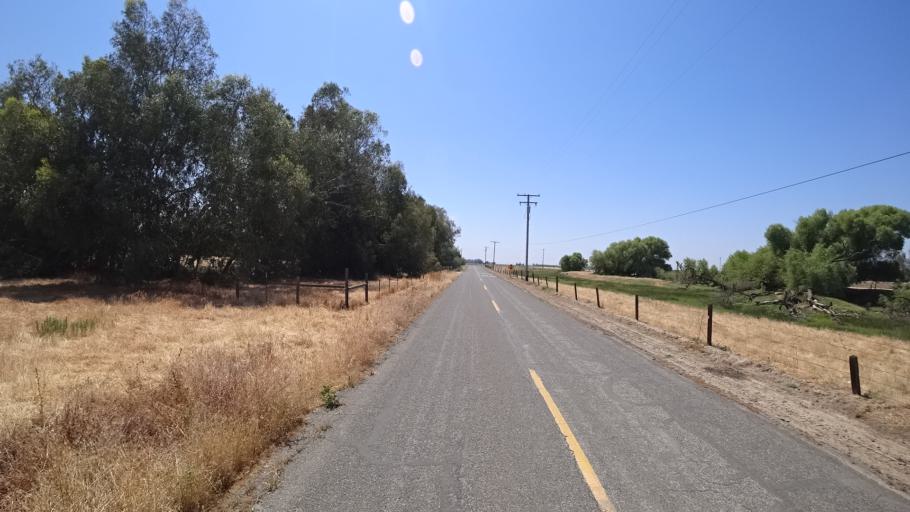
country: US
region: California
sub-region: Kings County
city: Armona
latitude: 36.2858
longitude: -119.6908
